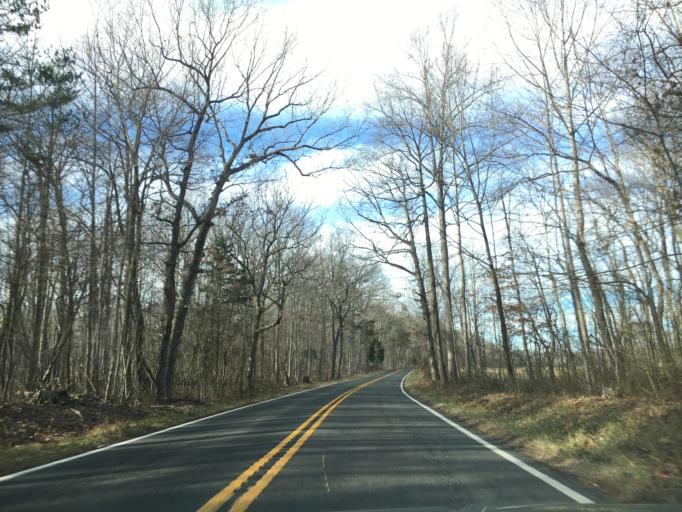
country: US
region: Virginia
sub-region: Fauquier County
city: Warrenton
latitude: 38.7318
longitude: -77.9502
